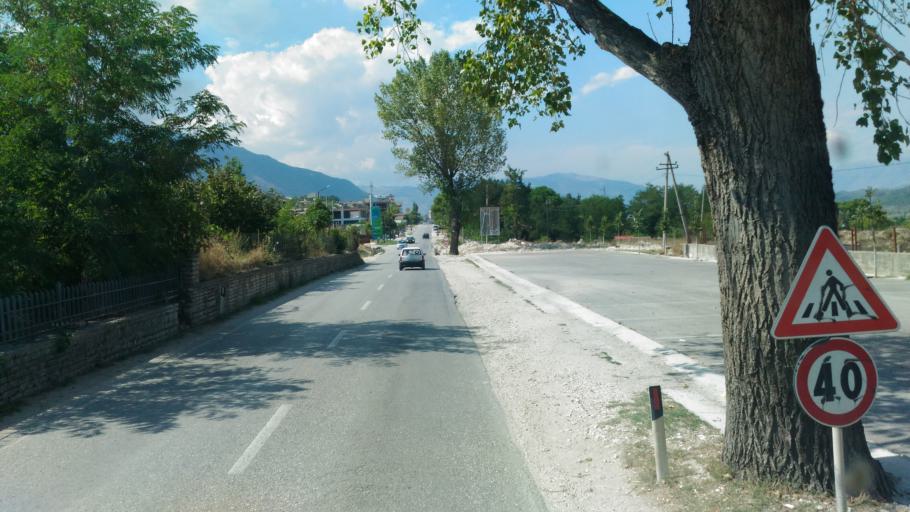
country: AL
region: Gjirokaster
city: Gjirokaster
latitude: 40.0695
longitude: 20.1606
